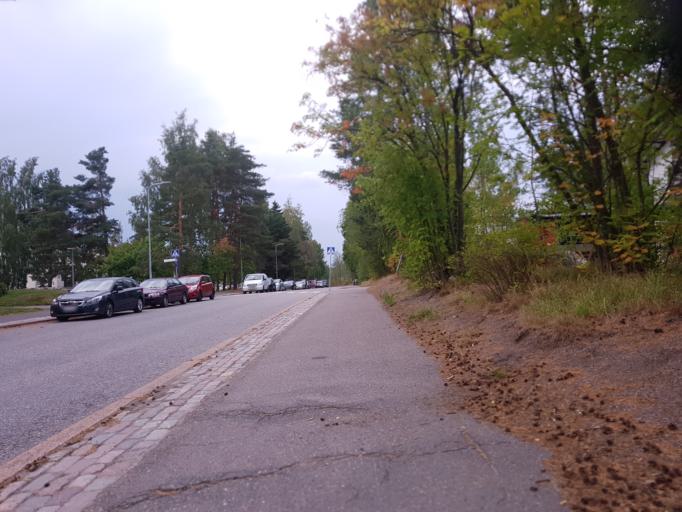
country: FI
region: Uusimaa
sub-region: Helsinki
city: Helsinki
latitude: 60.2316
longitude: 24.9509
